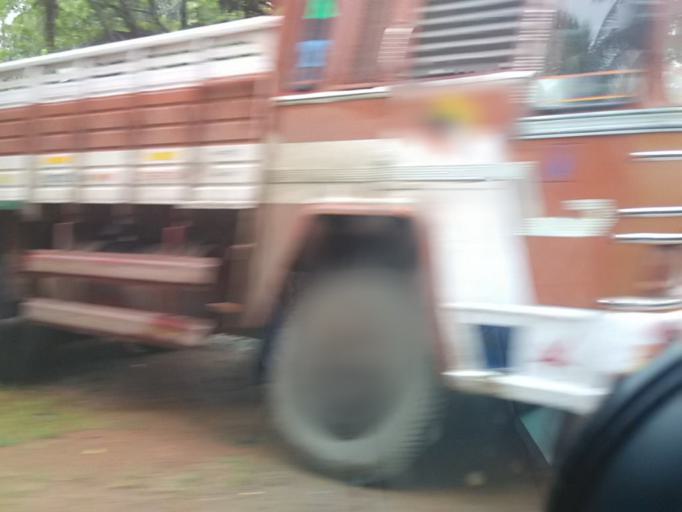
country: IN
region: Kerala
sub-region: Kozhikode
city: Kozhikode
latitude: 11.2755
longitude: 75.8126
